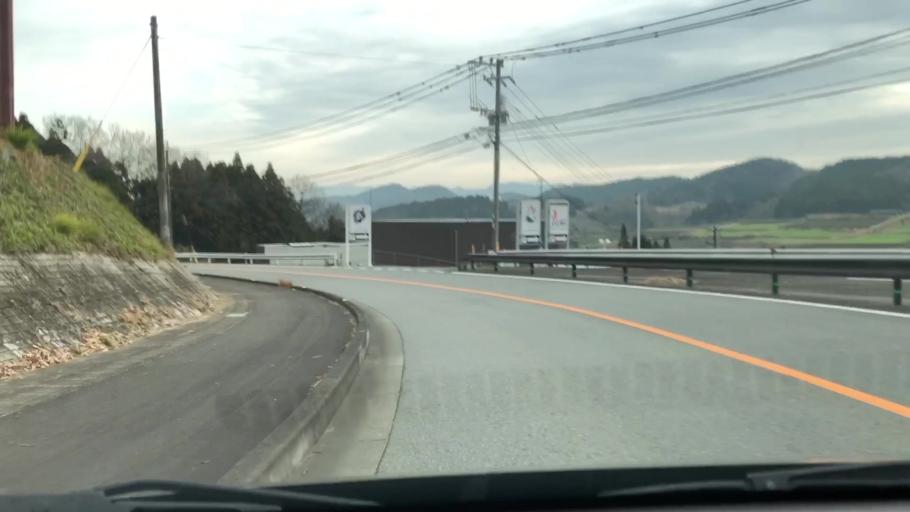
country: JP
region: Oita
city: Usuki
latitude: 33.0047
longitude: 131.6294
